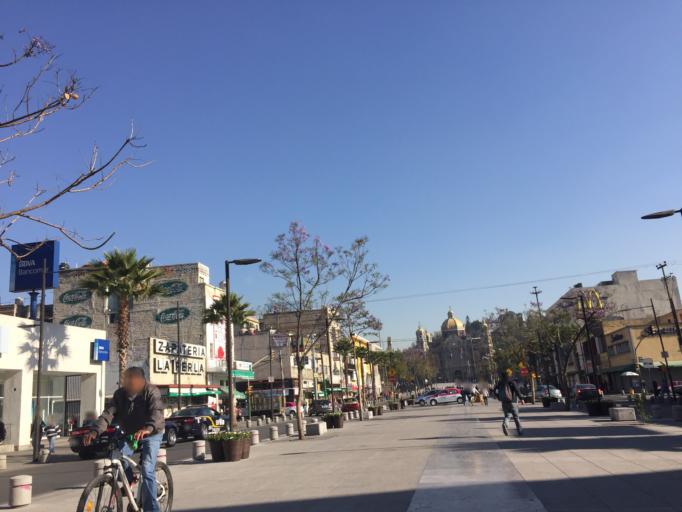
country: MX
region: Mexico
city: Colonia Lindavista
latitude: 19.4822
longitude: -99.1182
